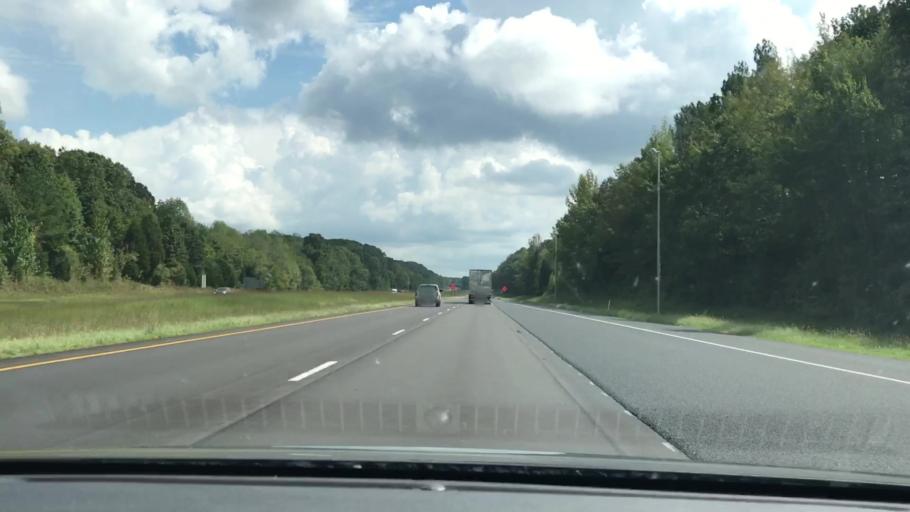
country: US
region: Tennessee
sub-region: Robertson County
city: Coopertown
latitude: 36.3456
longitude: -86.9272
